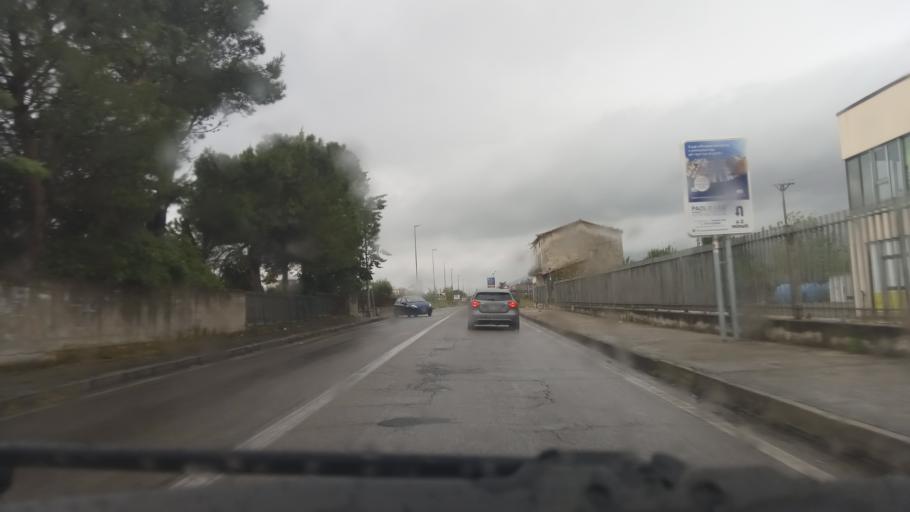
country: IT
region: Latium
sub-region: Provincia di Latina
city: Penitro
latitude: 41.2639
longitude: 13.6721
